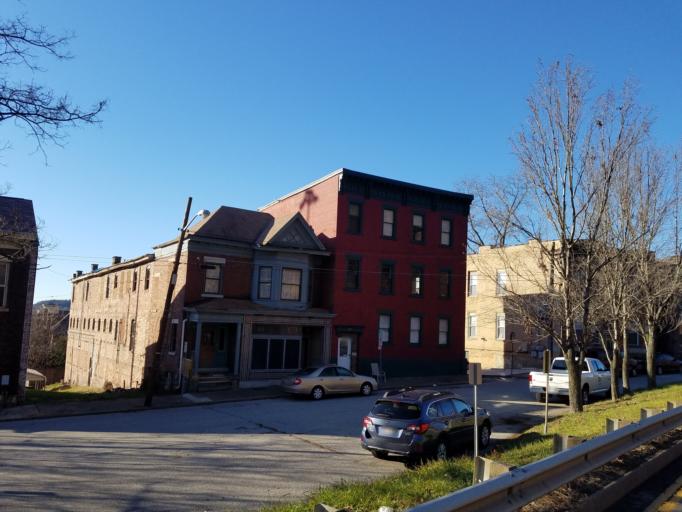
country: US
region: West Virginia
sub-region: Ohio County
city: Wheeling
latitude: 40.0724
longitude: -80.7227
